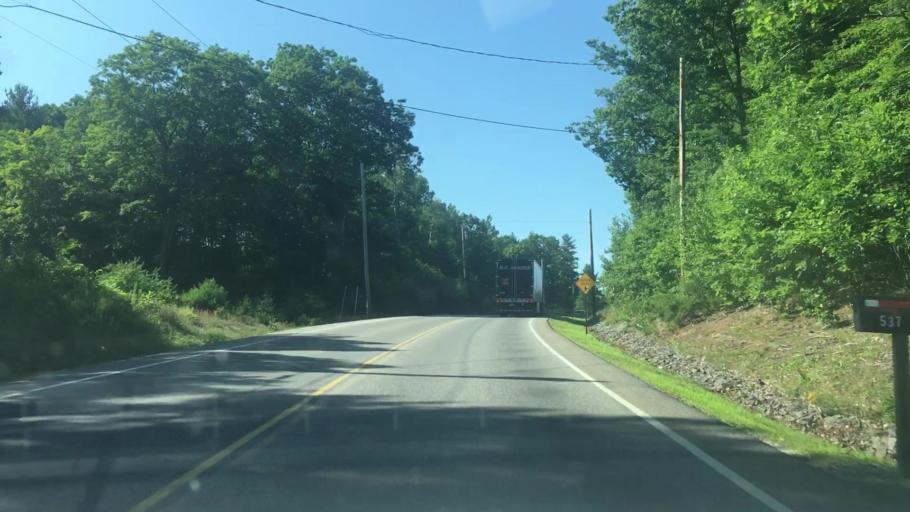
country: US
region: Maine
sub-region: York County
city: Buxton
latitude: 43.5803
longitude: -70.5170
